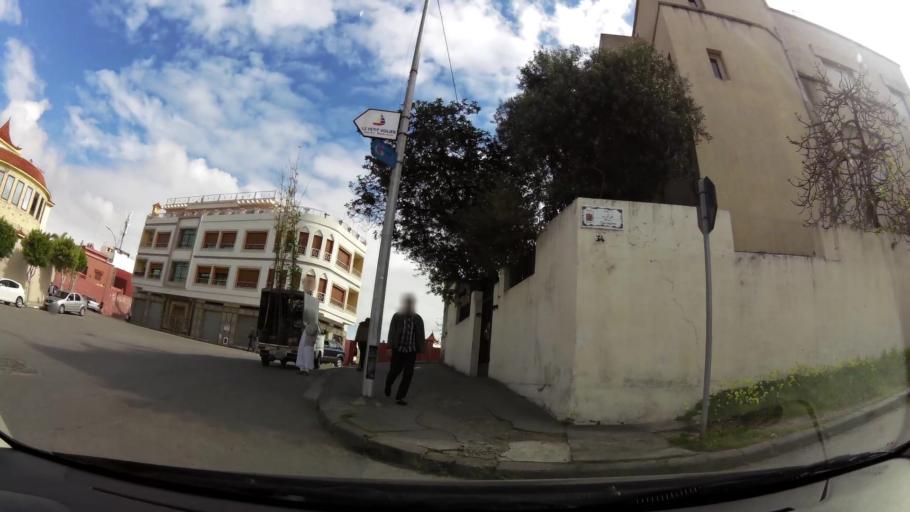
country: MA
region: Tanger-Tetouan
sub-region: Tanger-Assilah
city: Tangier
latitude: 35.7641
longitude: -5.8080
